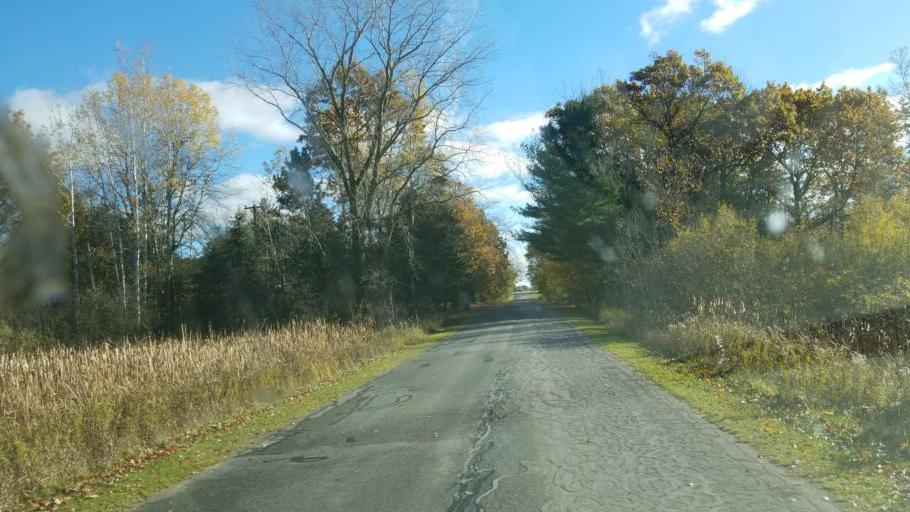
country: US
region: Michigan
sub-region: Montcalm County
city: Edmore
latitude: 43.4225
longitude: -85.0528
